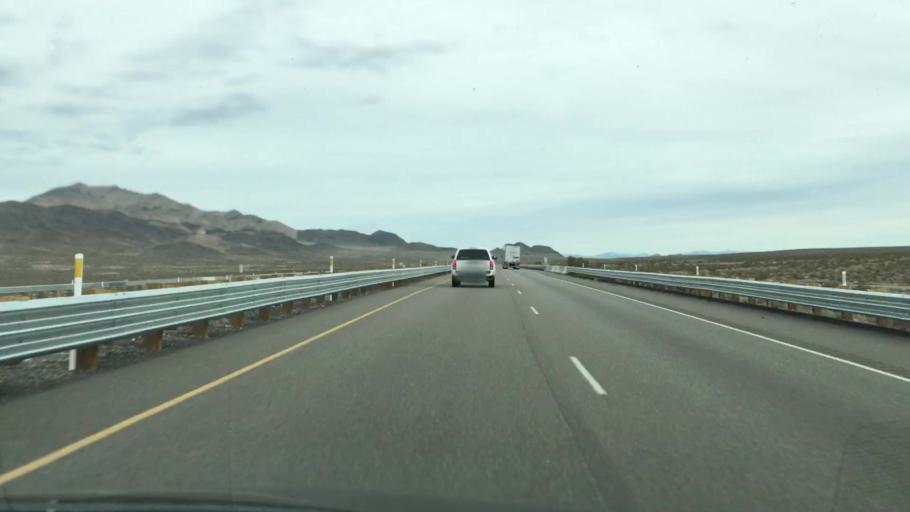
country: US
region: Nevada
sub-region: Nye County
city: Pahrump
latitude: 36.5978
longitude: -115.9989
